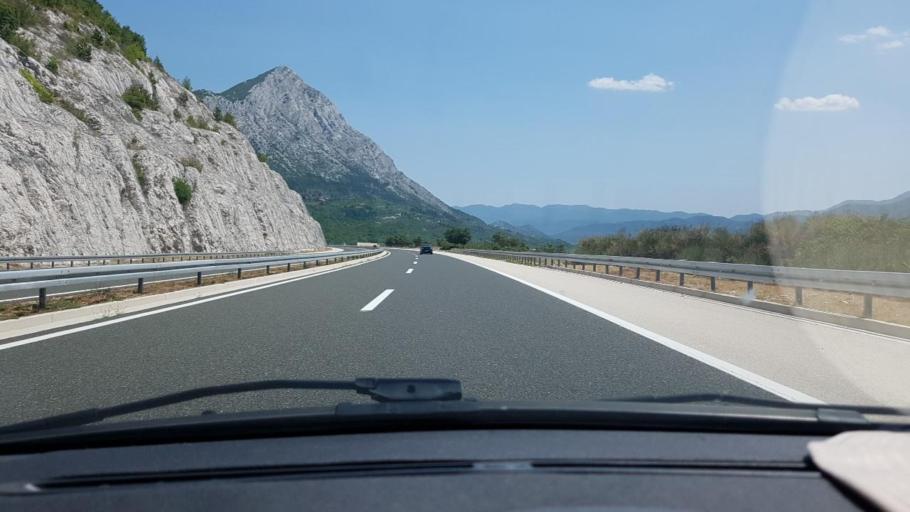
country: HR
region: Splitsko-Dalmatinska
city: Runovic
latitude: 43.2868
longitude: 17.2025
